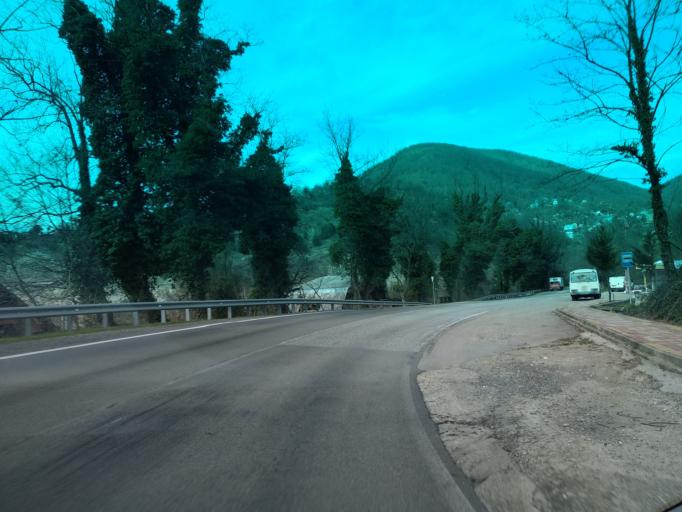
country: RU
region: Krasnodarskiy
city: Tuapse
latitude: 44.0858
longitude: 39.1286
